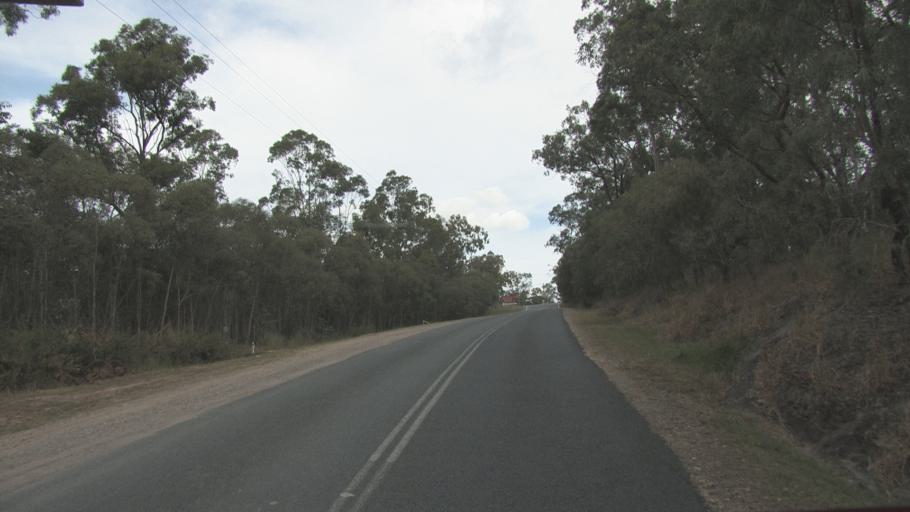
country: AU
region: Queensland
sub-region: Logan
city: Windaroo
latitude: -27.7243
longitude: 153.1737
